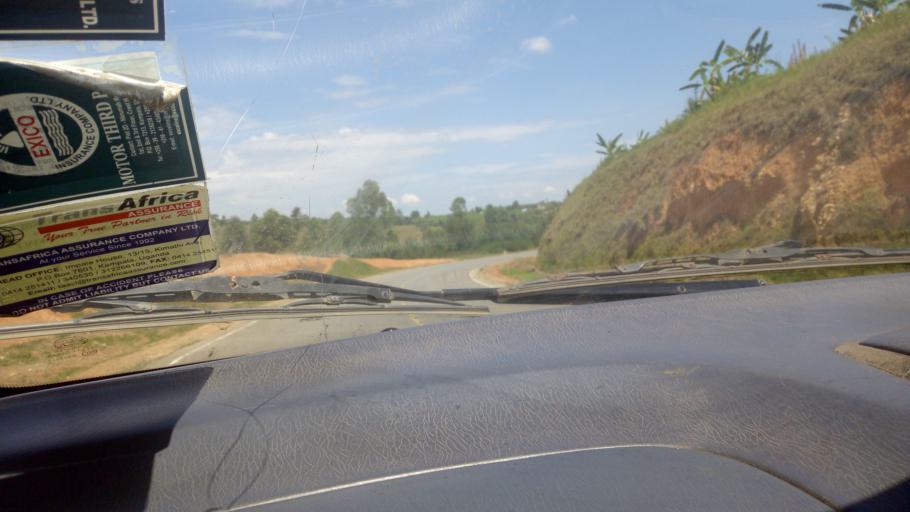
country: UG
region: Western Region
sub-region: Buhweju District
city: Buhweju
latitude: -0.2805
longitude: 30.5609
